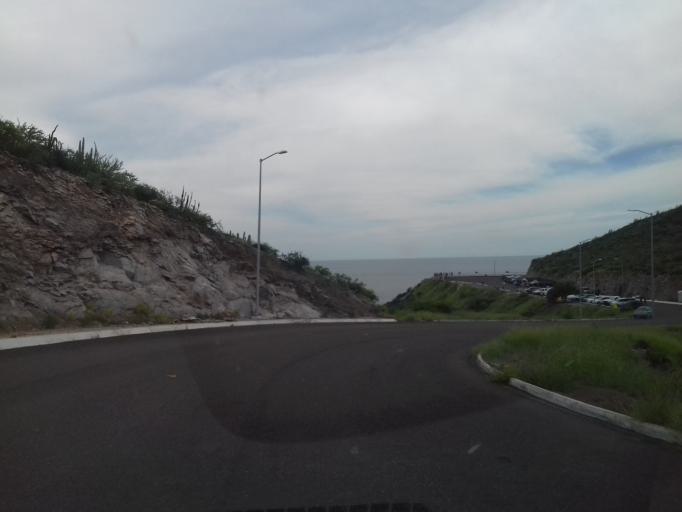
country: MX
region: Sonora
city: Heroica Guaymas
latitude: 27.9391
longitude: -111.0971
